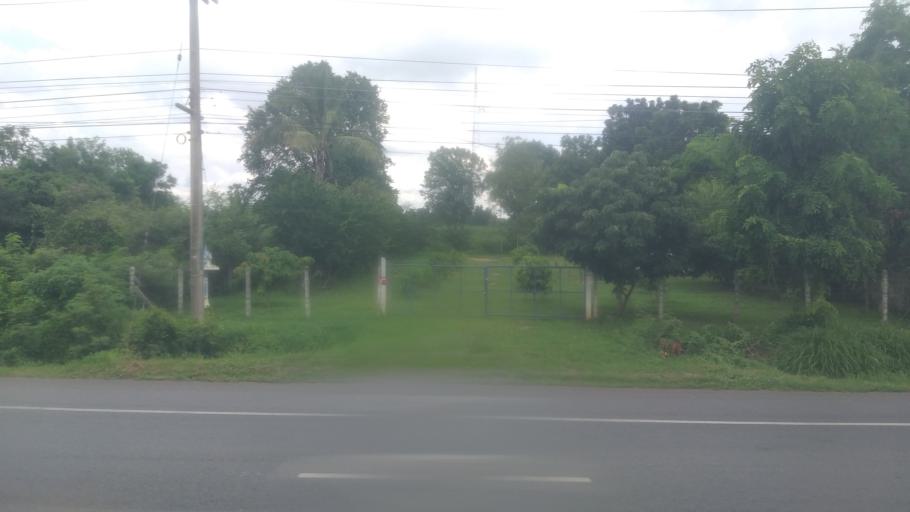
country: TH
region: Chaiyaphum
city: Noen Sa-nga
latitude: 15.6712
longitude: 101.9604
